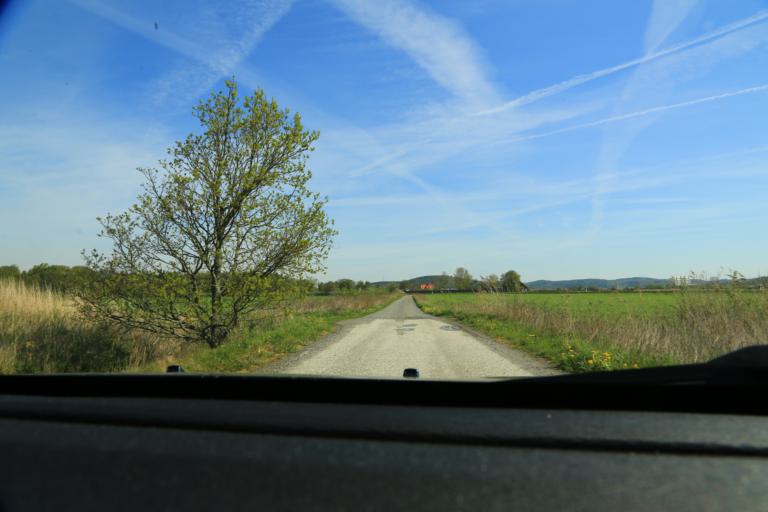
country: SE
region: Halland
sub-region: Varbergs Kommun
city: Varberg
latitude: 57.1486
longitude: 12.2667
